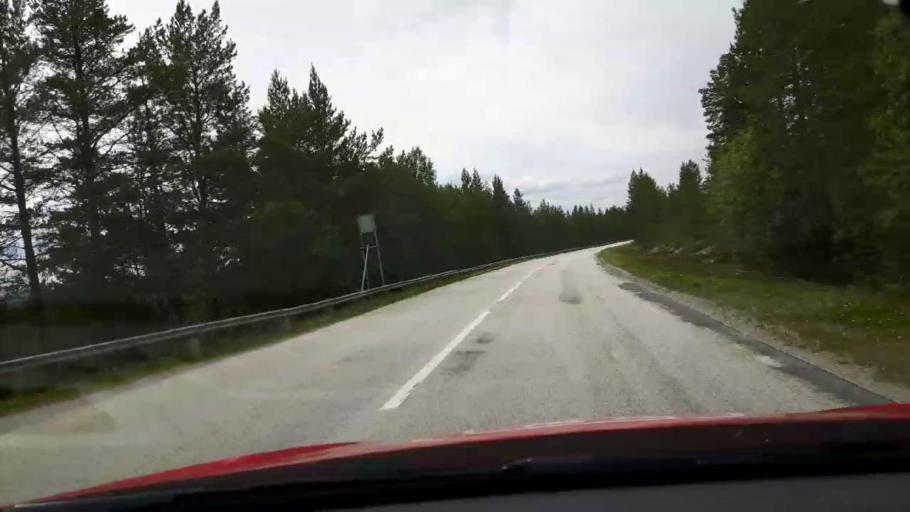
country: SE
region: Jaemtland
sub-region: Harjedalens Kommun
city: Sveg
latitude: 62.4114
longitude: 13.6536
